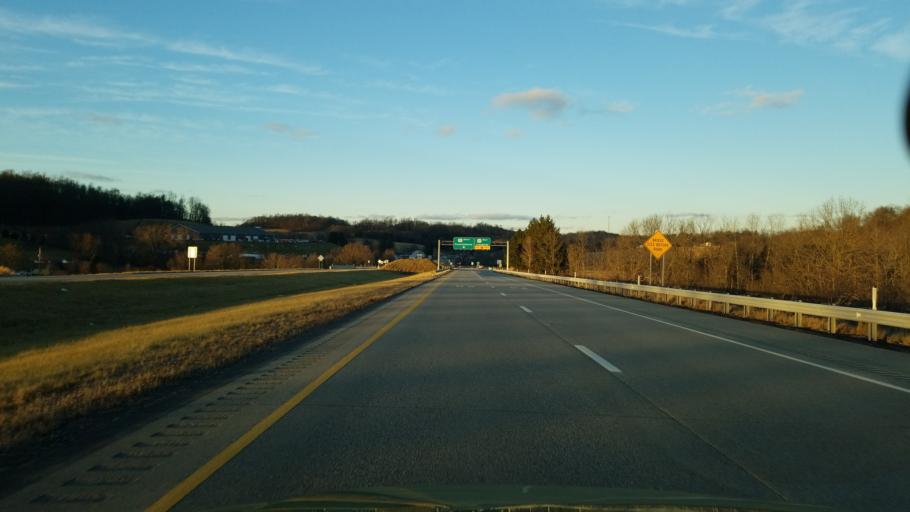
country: US
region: Pennsylvania
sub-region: Indiana County
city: Chevy Chase Heights
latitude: 40.6655
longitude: -79.1135
